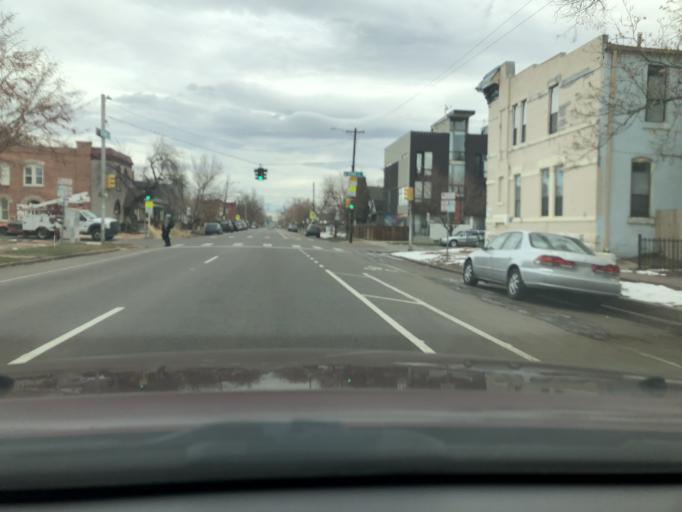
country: US
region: Colorado
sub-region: Denver County
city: Denver
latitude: 39.7568
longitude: -104.9790
